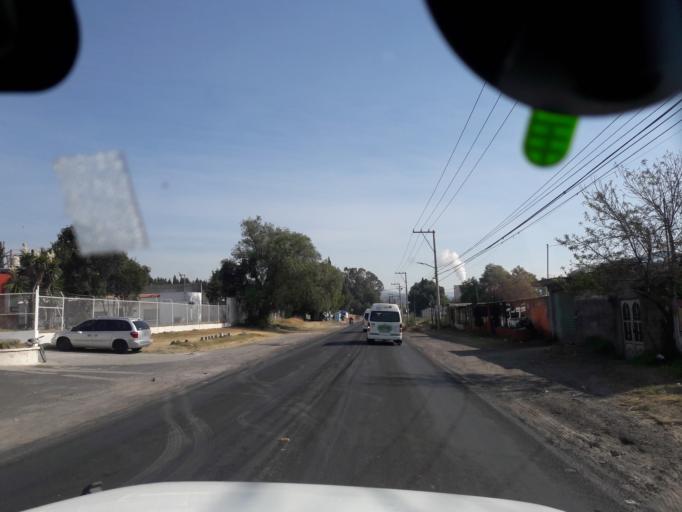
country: MX
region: Tlaxcala
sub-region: Ixtacuixtla de Mariano Matamoros
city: Villa Mariano Matamoros
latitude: 19.3007
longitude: -98.3986
